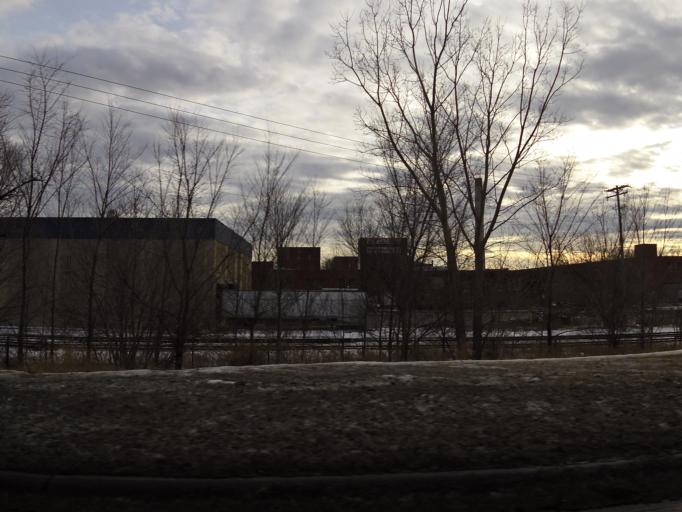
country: US
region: Minnesota
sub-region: Ramsey County
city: Saint Paul
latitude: 44.9657
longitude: -93.0712
